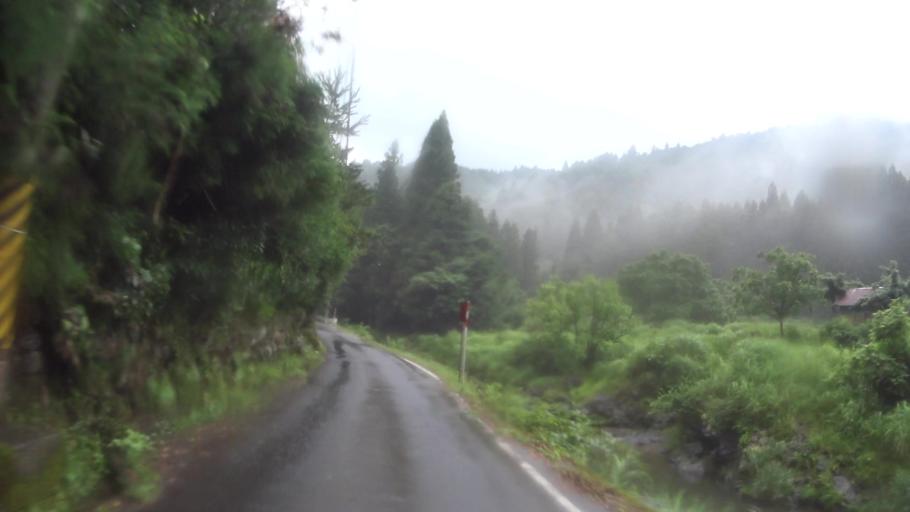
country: JP
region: Shiga Prefecture
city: Kitahama
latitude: 35.2646
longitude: 135.8220
